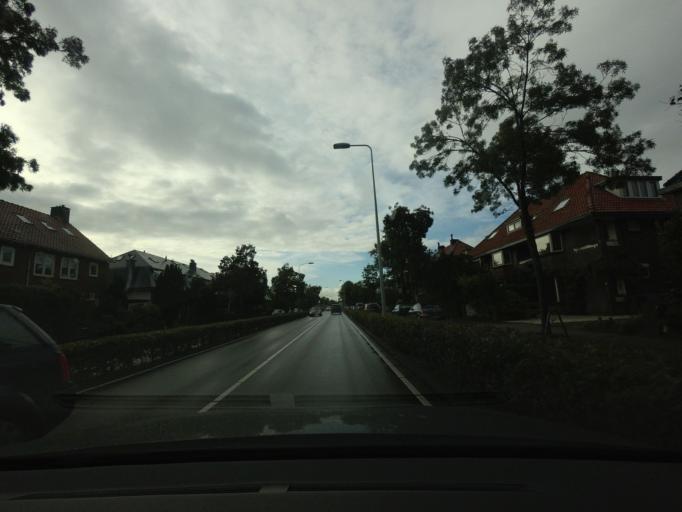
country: NL
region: South Holland
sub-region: Gemeente Voorschoten
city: Voorschoten
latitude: 52.1263
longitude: 4.4404
